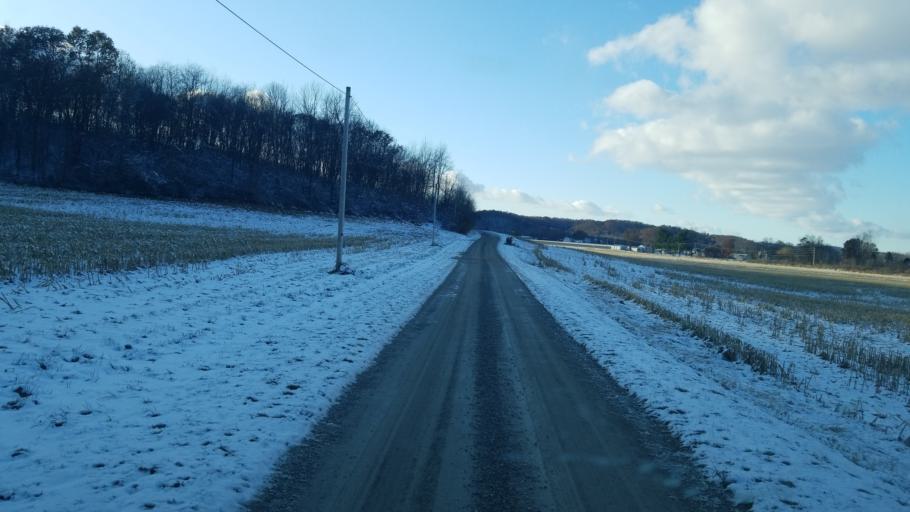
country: US
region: Ohio
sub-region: Licking County
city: Utica
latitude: 40.1666
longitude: -82.4024
